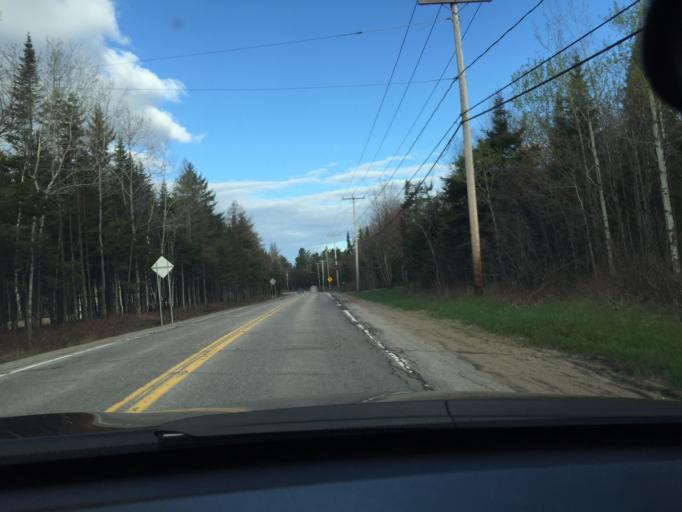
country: CA
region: Quebec
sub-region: Capitale-Nationale
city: Sainte Catherine de la Jacques Cartier
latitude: 46.8505
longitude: -71.5701
